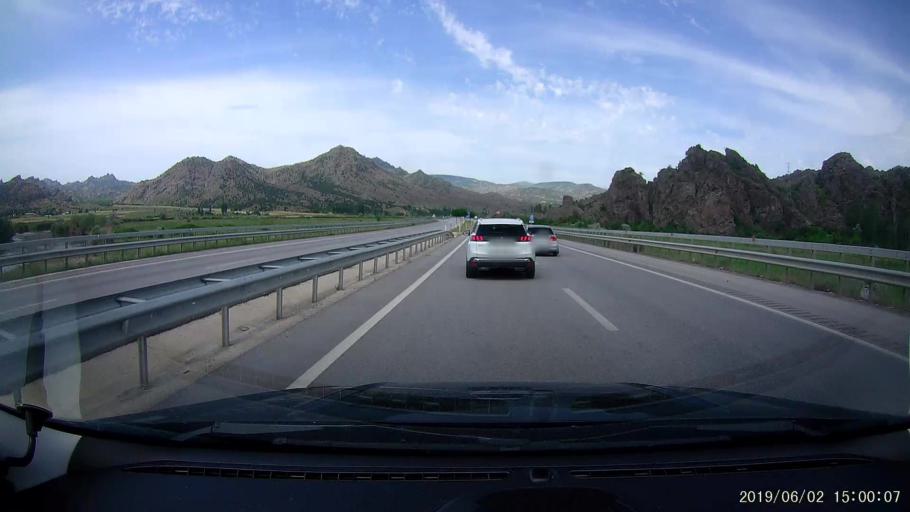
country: TR
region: Corum
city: Osmancik
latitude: 40.9743
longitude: 34.7075
